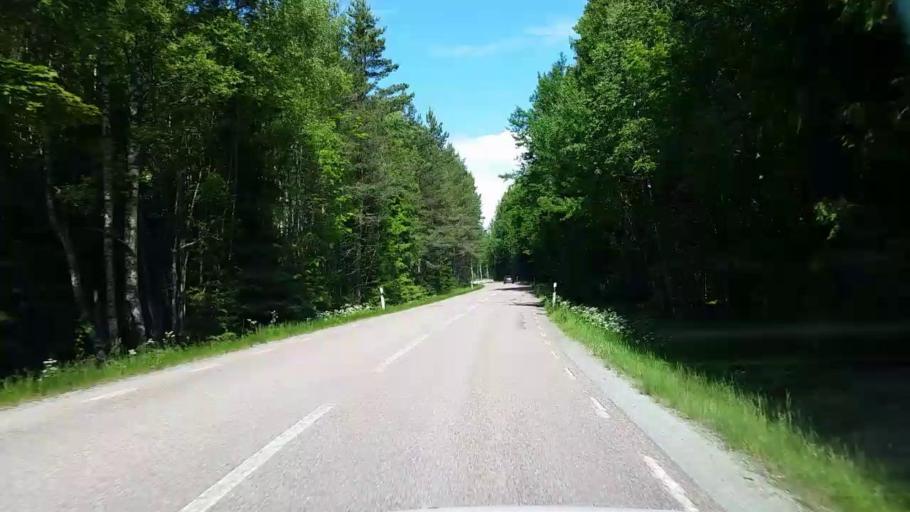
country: SE
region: Vaestmanland
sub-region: Fagersta Kommun
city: Fagersta
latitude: 59.9533
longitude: 15.7860
